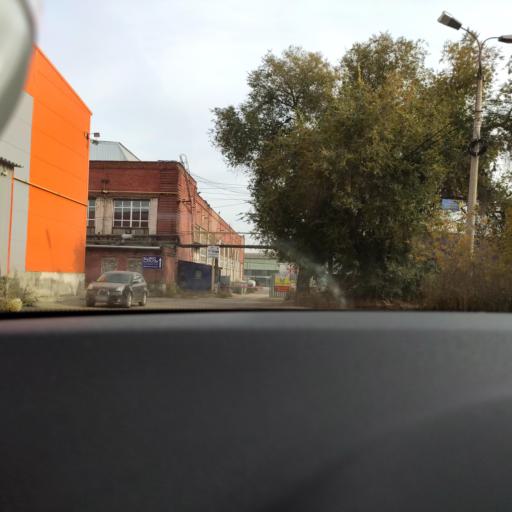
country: RU
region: Samara
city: Samara
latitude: 53.1922
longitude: 50.2460
